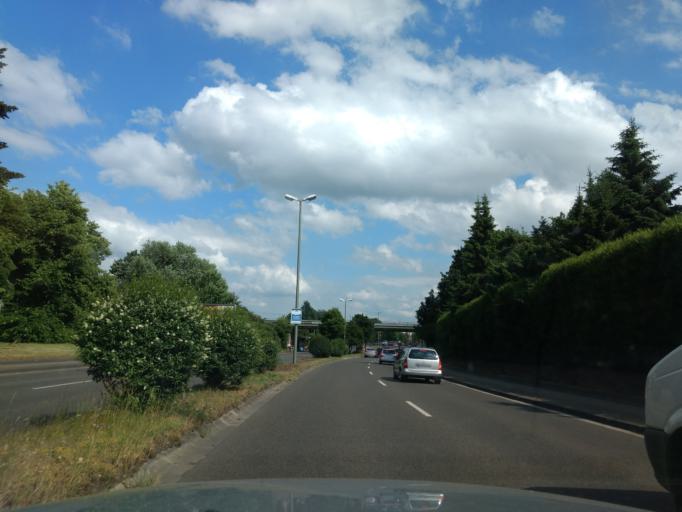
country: DE
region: North Rhine-Westphalia
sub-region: Regierungsbezirk Dusseldorf
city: Neuss
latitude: 51.1844
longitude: 6.6751
